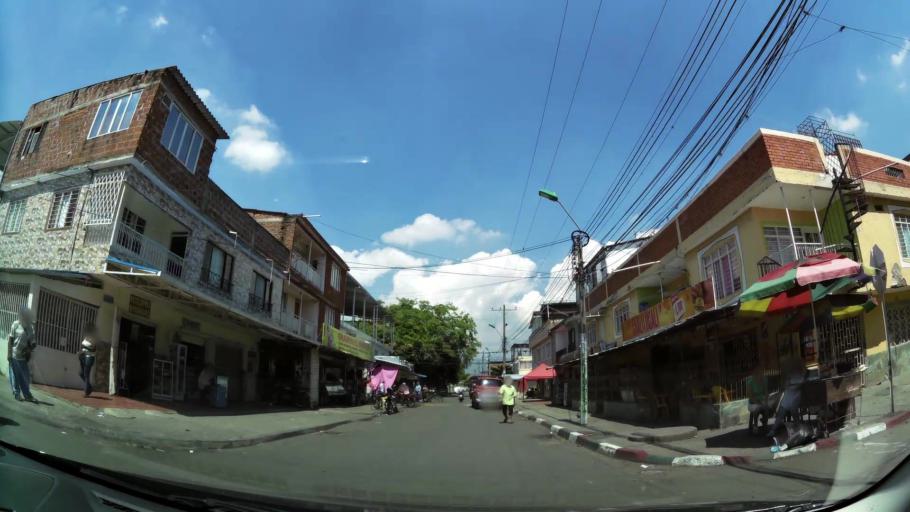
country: CO
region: Valle del Cauca
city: Cali
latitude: 3.4281
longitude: -76.5021
